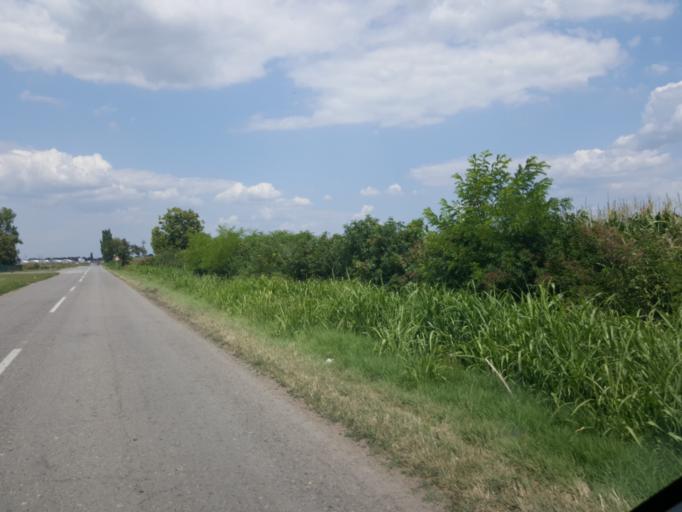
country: RS
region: Autonomna Pokrajina Vojvodina
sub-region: Sremski Okrug
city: Pecinci
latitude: 44.8834
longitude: 19.9606
